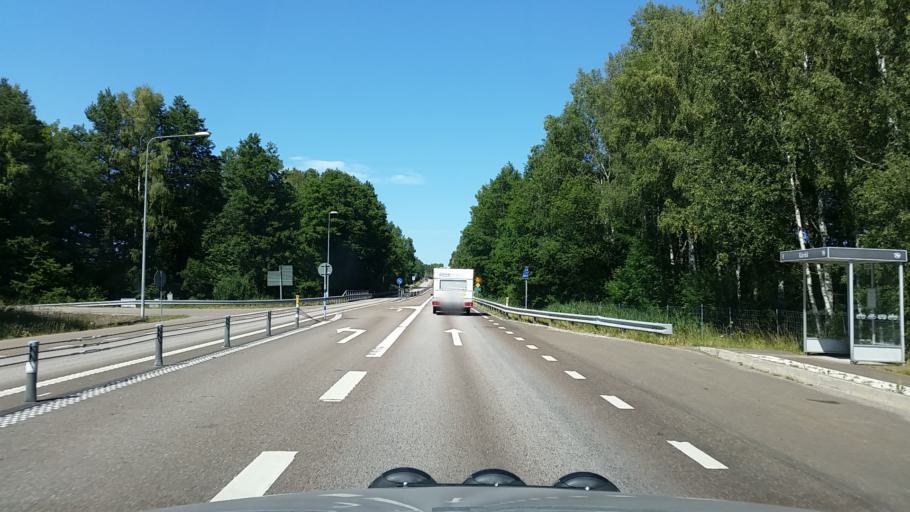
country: SE
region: Vaestra Goetaland
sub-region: Melleruds Kommun
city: Mellerud
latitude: 58.8140
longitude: 12.5236
